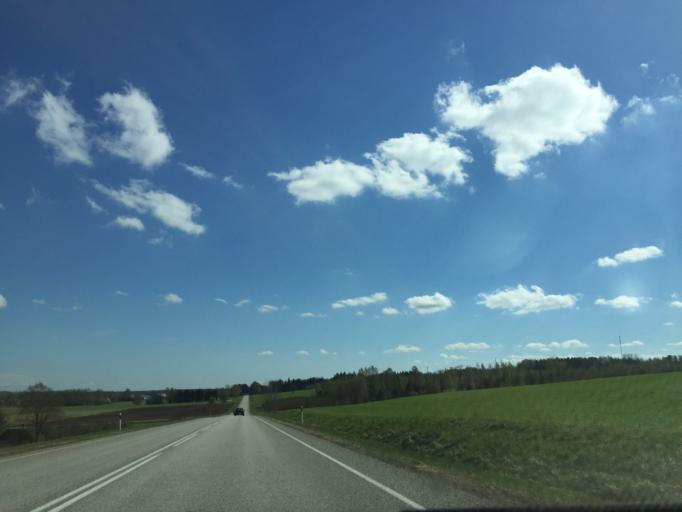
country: EE
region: Valgamaa
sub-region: Valga linn
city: Valga
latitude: 57.9008
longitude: 26.0499
